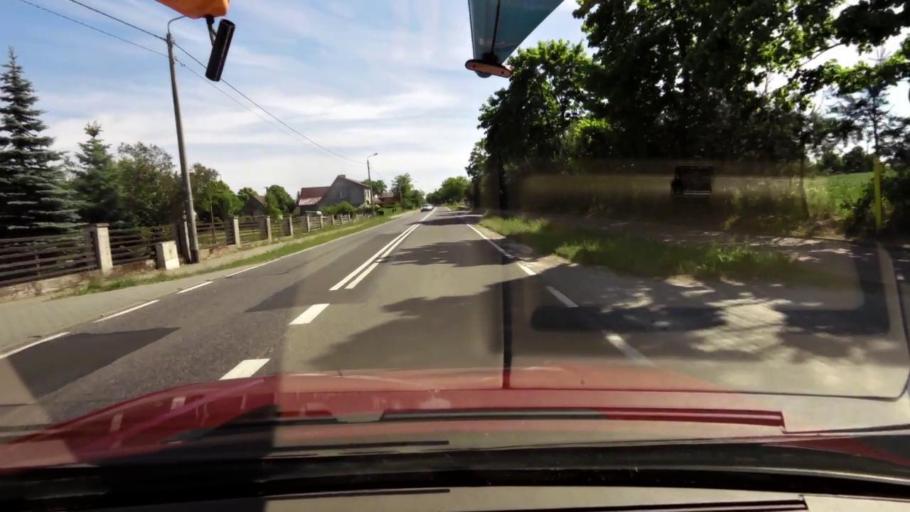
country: PL
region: Pomeranian Voivodeship
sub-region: Powiat slupski
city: Kobylnica
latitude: 54.4129
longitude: 17.0078
